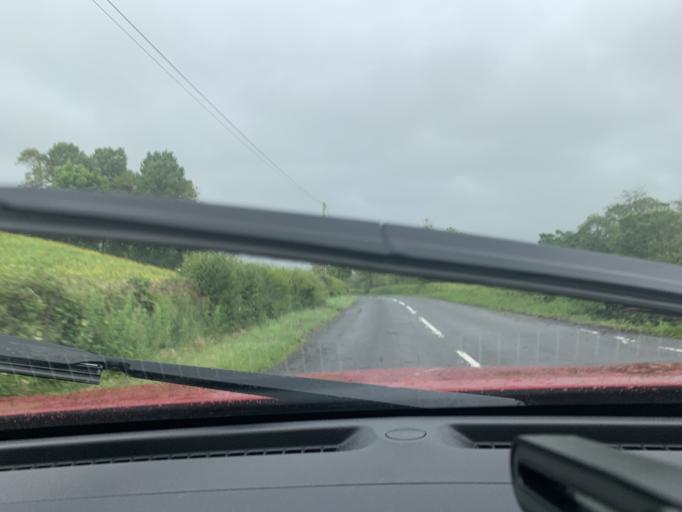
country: GB
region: Northern Ireland
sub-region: Fermanagh District
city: Enniskillen
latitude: 54.3059
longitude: -7.6863
